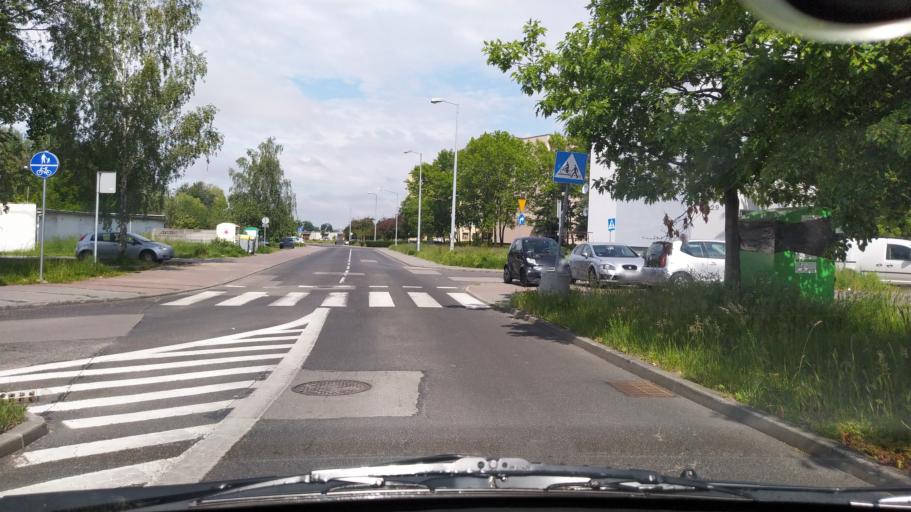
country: PL
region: Silesian Voivodeship
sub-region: Powiat gliwicki
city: Przyszowice
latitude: 50.2814
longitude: 18.7350
